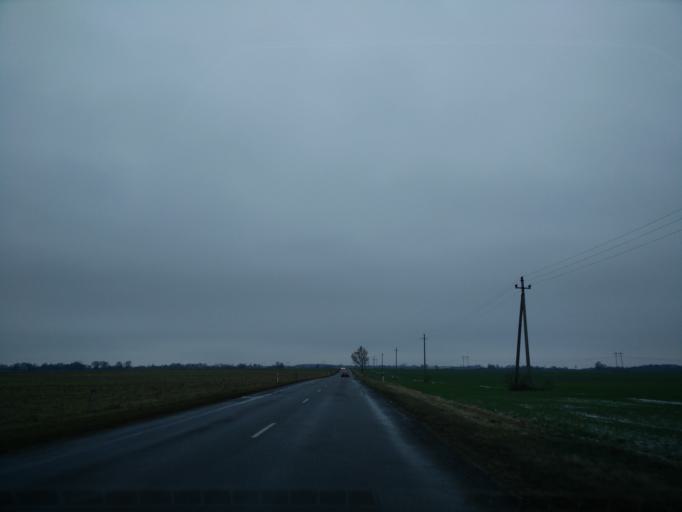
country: LT
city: Ariogala
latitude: 55.3087
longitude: 23.4323
